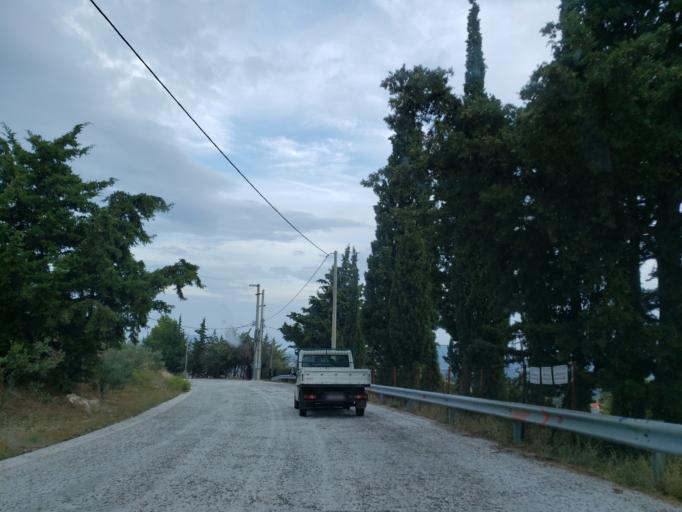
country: GR
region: Attica
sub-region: Nomarchia Anatolikis Attikis
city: Grammatiko
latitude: 38.2049
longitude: 23.9553
